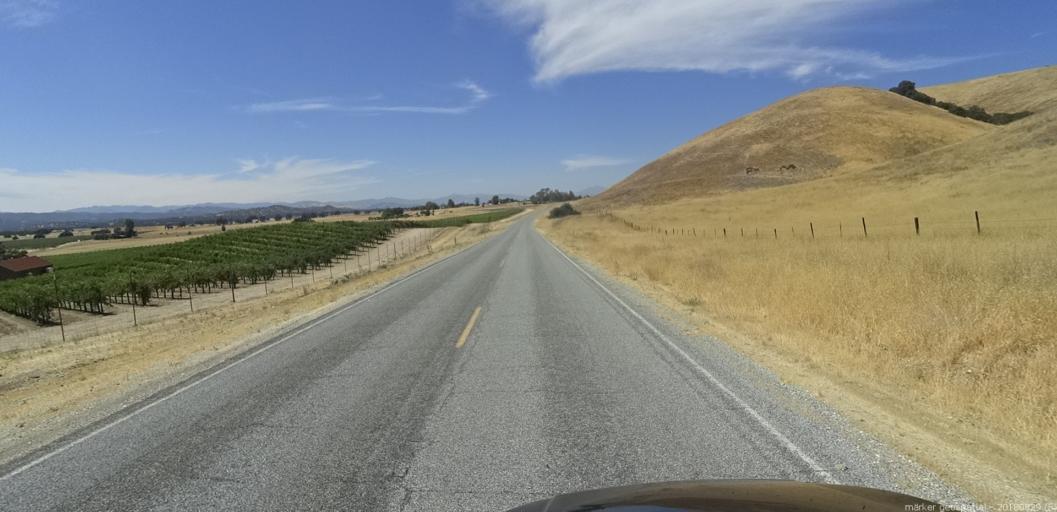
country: US
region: California
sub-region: San Luis Obispo County
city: Lake Nacimiento
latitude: 35.9097
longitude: -121.0166
